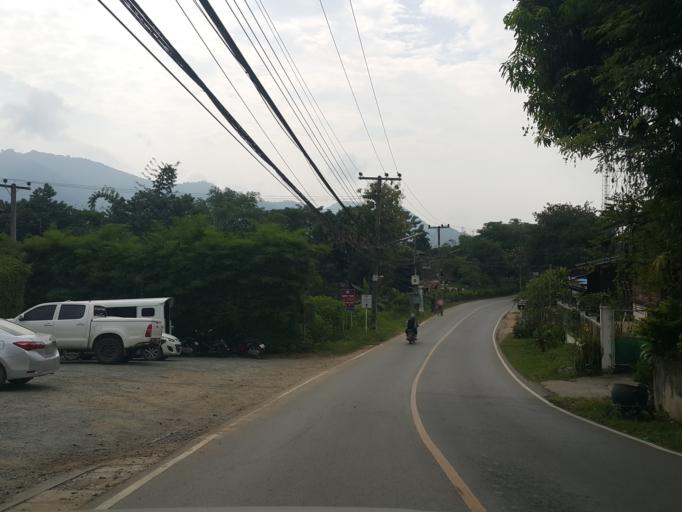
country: TH
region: Chiang Mai
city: Pai
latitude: 19.3678
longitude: 98.4389
